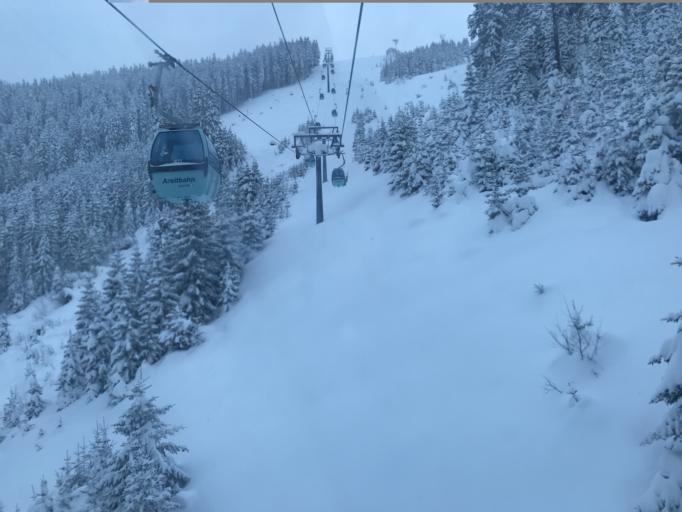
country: AT
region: Salzburg
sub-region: Politischer Bezirk Zell am See
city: Kaprun
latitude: 47.3126
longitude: 12.7561
